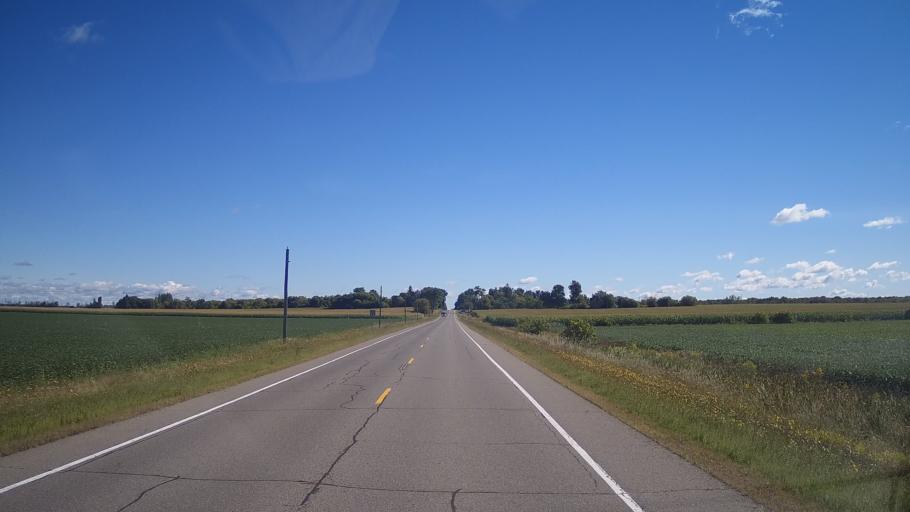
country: US
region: New York
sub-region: St. Lawrence County
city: Ogdensburg
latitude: 44.9364
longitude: -75.3169
